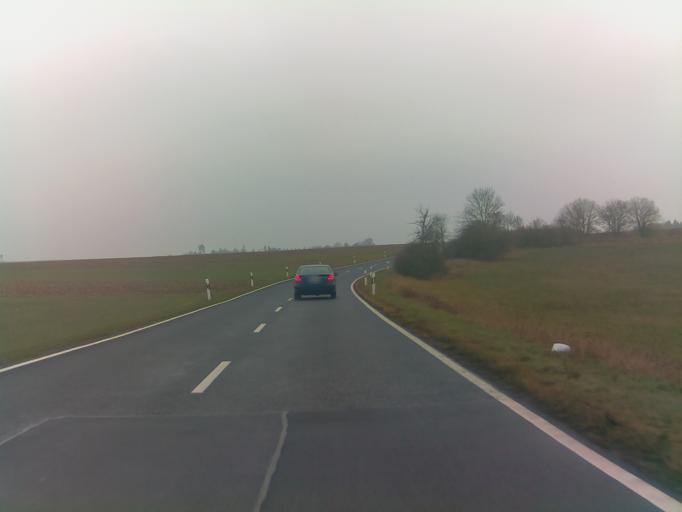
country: DE
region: Thuringia
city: Leutersdorf
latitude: 50.4876
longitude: 10.5680
